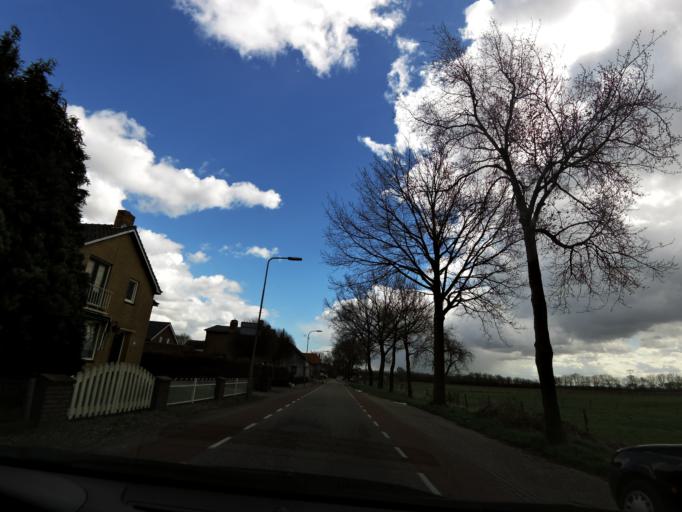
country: BE
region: Flanders
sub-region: Provincie Limburg
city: Maaseik
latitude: 51.1110
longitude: 5.8364
